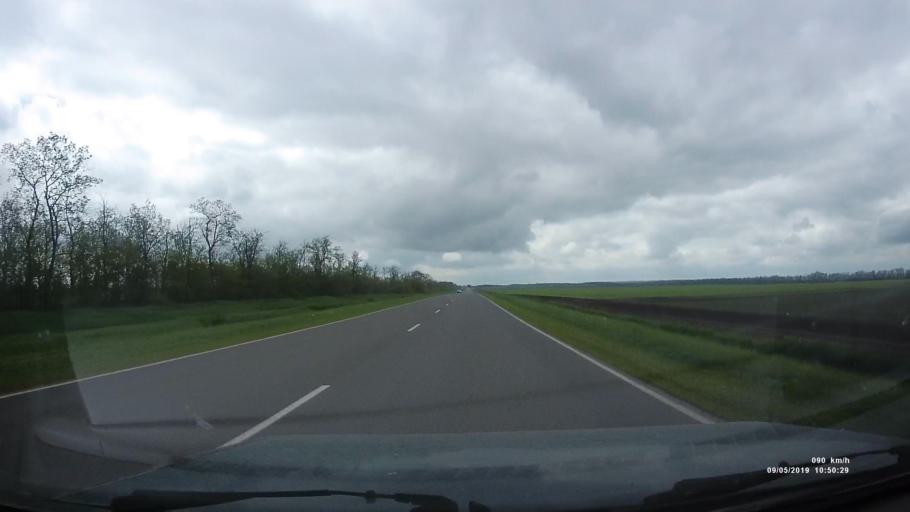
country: RU
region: Rostov
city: Peshkovo
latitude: 46.9281
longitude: 39.3554
